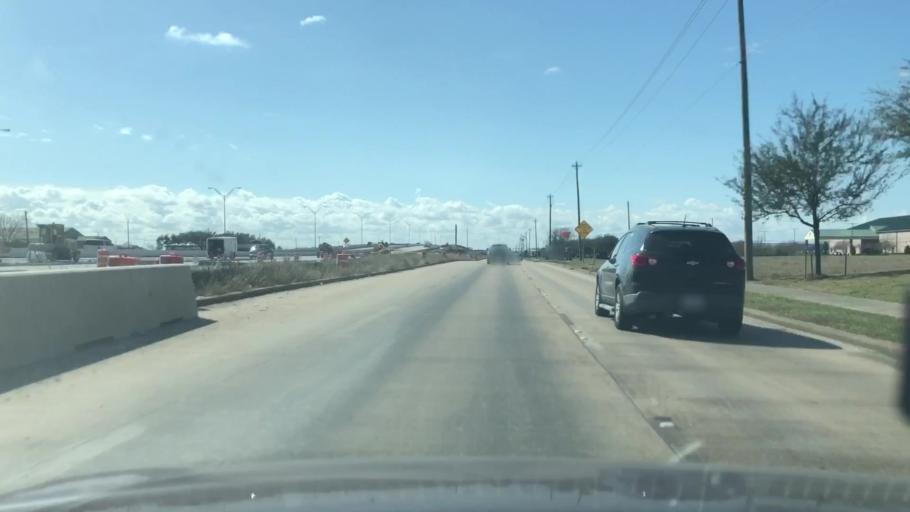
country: US
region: Texas
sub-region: Harris County
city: Pasadena
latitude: 29.6376
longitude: -95.1643
